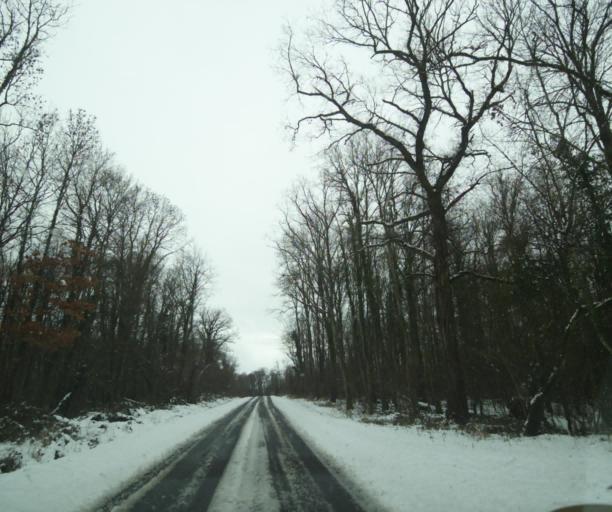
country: FR
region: Champagne-Ardenne
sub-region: Departement de la Haute-Marne
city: Montier-en-Der
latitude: 48.4232
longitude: 4.7281
